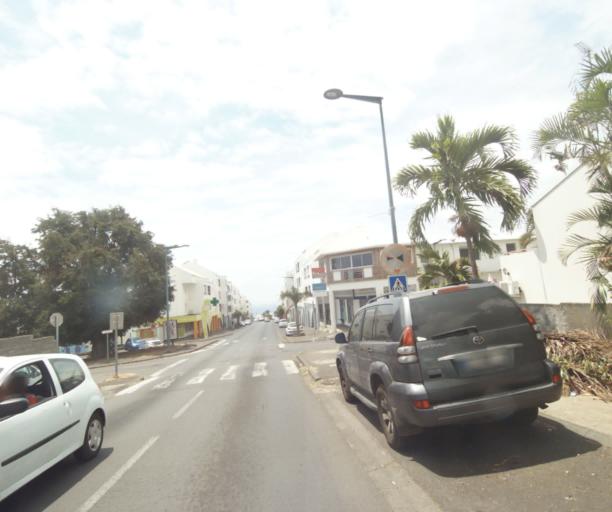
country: RE
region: Reunion
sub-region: Reunion
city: Saint-Paul
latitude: -21.0249
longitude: 55.2660
